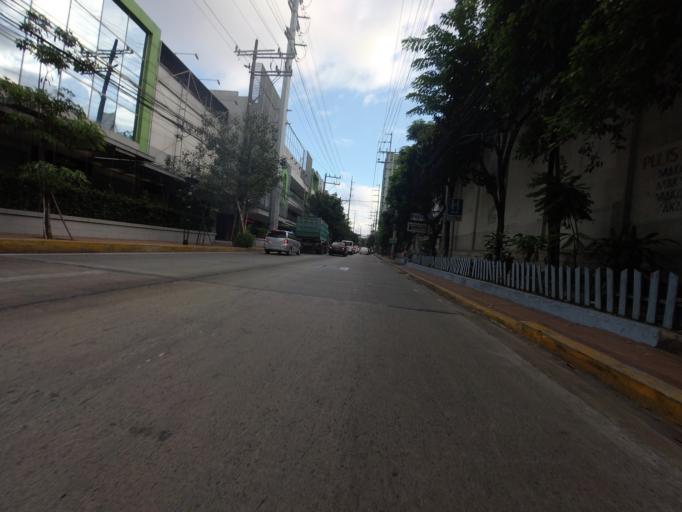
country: PH
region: Metro Manila
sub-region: City of Manila
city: Quiapo
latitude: 14.5842
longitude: 120.9867
